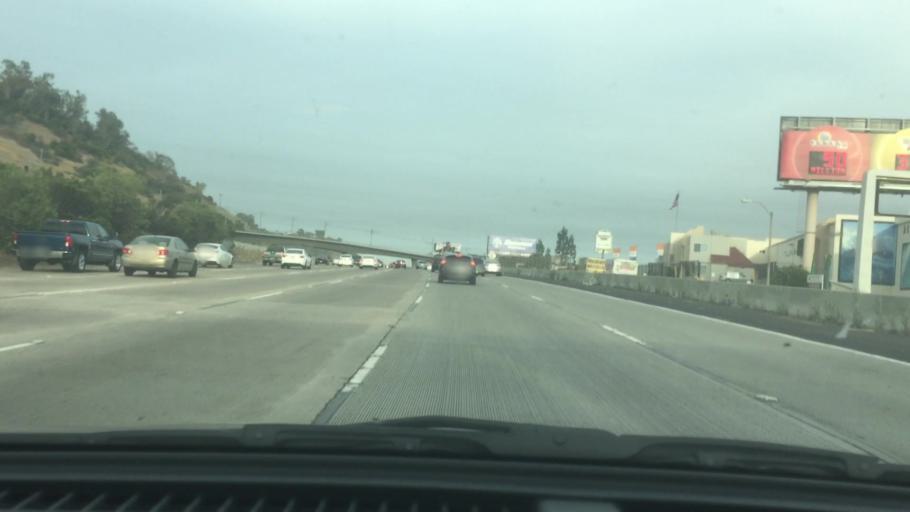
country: US
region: California
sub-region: San Diego County
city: La Mesa
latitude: 32.7807
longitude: -117.0922
